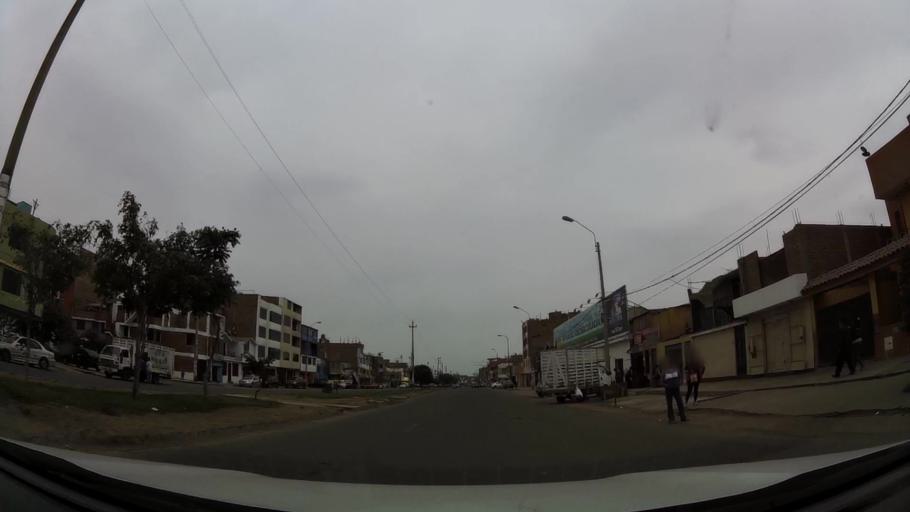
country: PE
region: Lima
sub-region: Lima
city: Independencia
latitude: -11.9790
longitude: -77.0844
